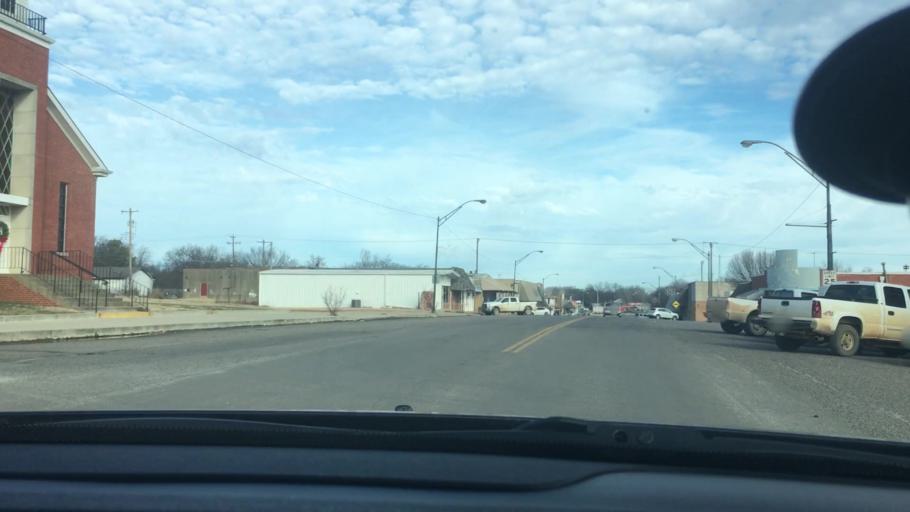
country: US
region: Oklahoma
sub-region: Seminole County
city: Konawa
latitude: 34.9560
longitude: -96.7521
